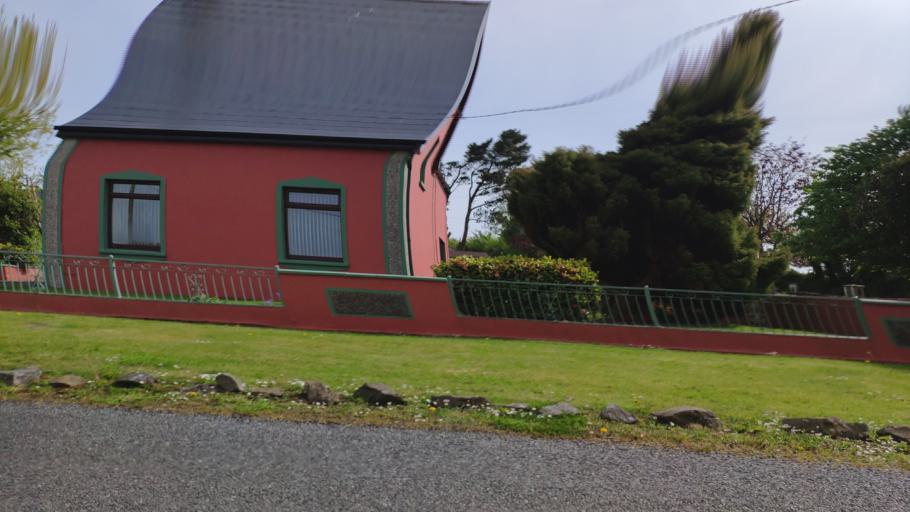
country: IE
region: Munster
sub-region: County Cork
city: Blarney
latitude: 51.9562
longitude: -8.5083
